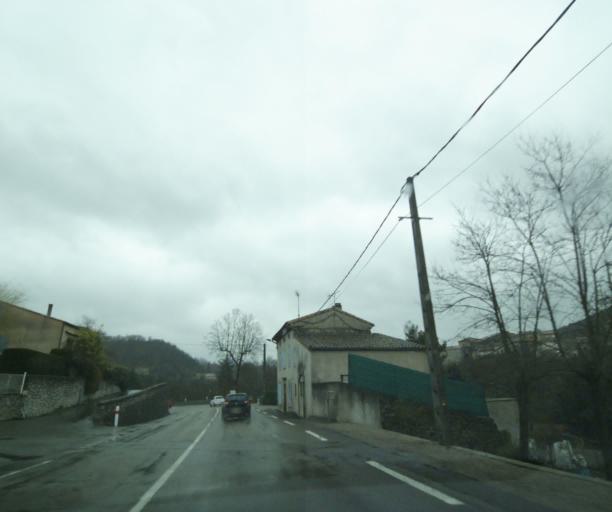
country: FR
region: Rhone-Alpes
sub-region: Departement de l'Ardeche
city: Coux
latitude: 44.7349
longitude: 4.6178
